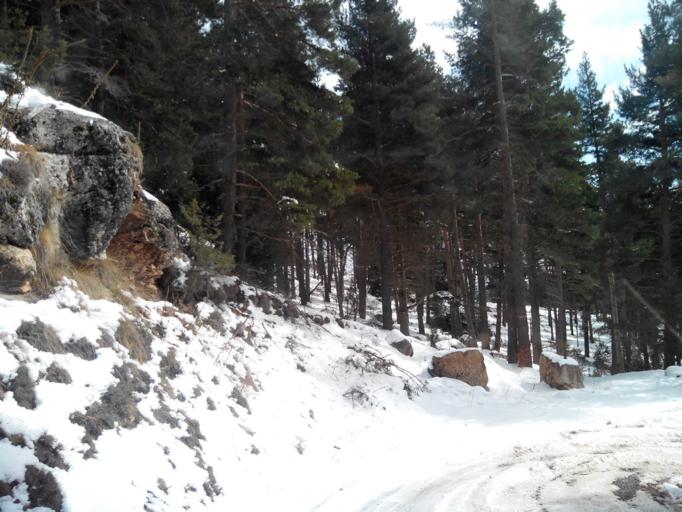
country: ES
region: Catalonia
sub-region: Provincia de Barcelona
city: Sant Julia de Cerdanyola
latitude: 42.1947
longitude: 1.9280
